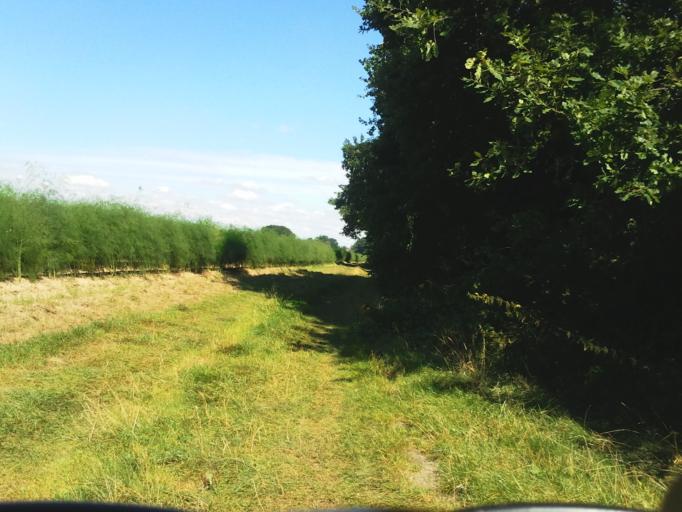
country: DE
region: Lower Saxony
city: Nienburg
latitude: 52.6511
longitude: 9.2374
